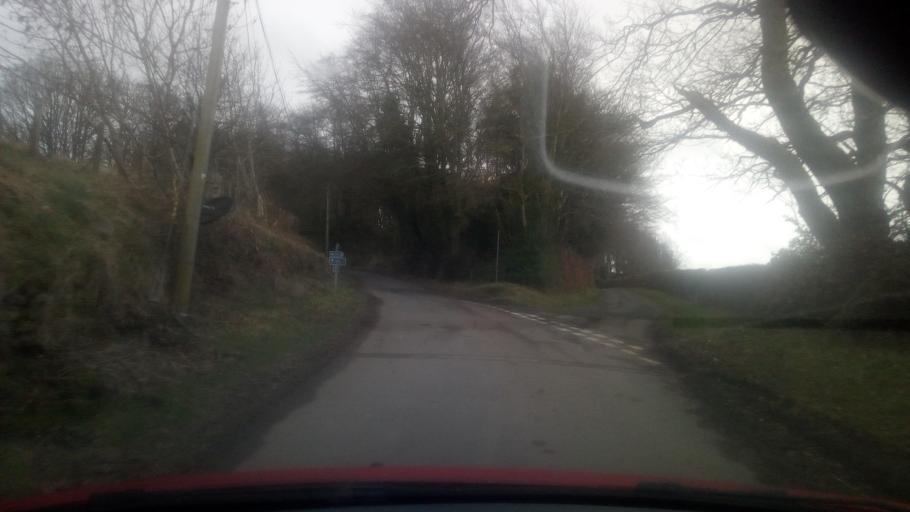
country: GB
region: Scotland
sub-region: The Scottish Borders
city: Jedburgh
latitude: 55.4707
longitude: -2.5376
